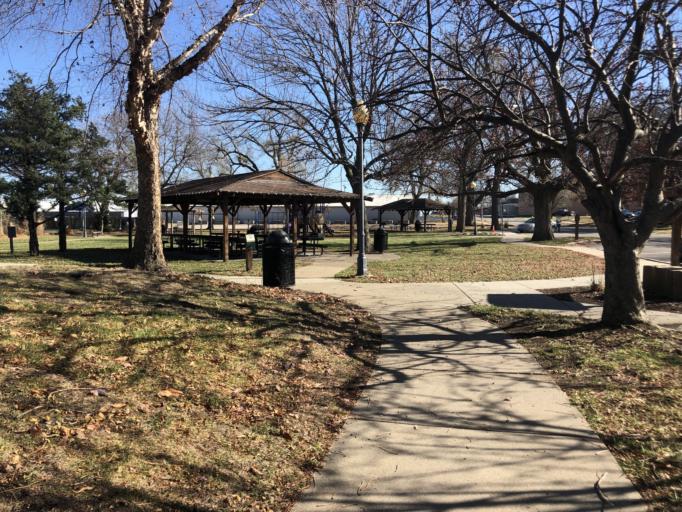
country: US
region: Kansas
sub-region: Johnson County
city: Gardner
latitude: 38.8130
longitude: -94.9268
